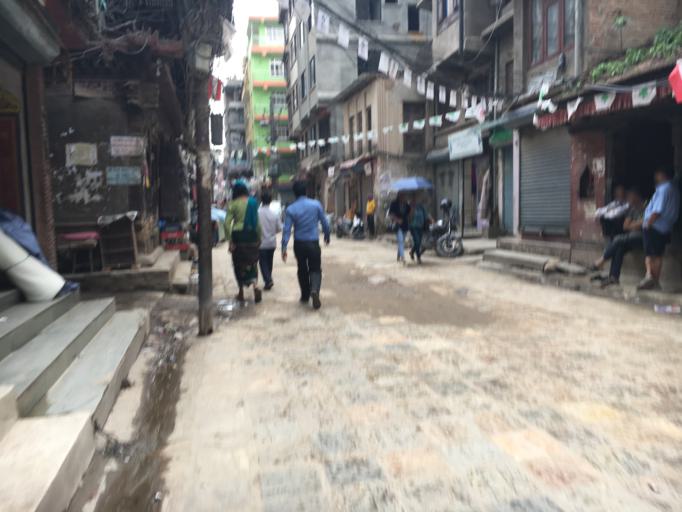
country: NP
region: Central Region
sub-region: Bagmati Zone
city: Kathmandu
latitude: 27.7088
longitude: 85.3104
